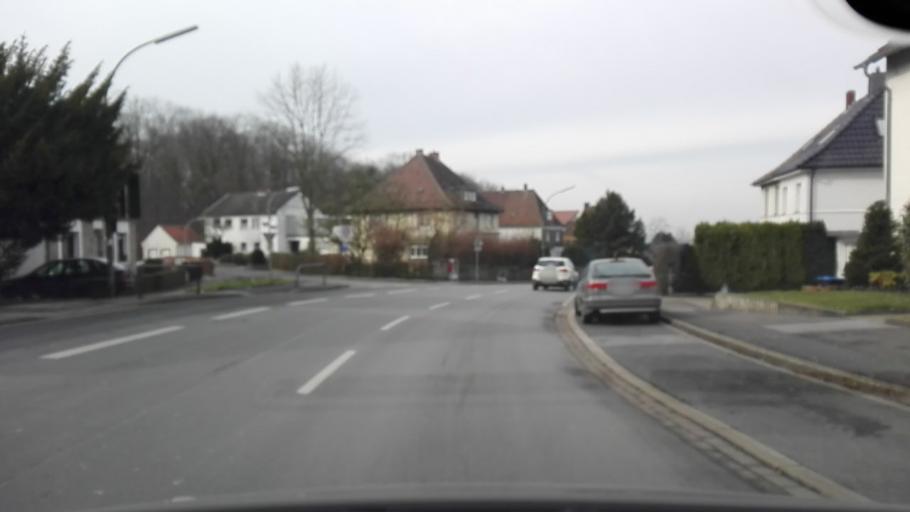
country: DE
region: North Rhine-Westphalia
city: Schwerte
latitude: 51.4645
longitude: 7.5226
